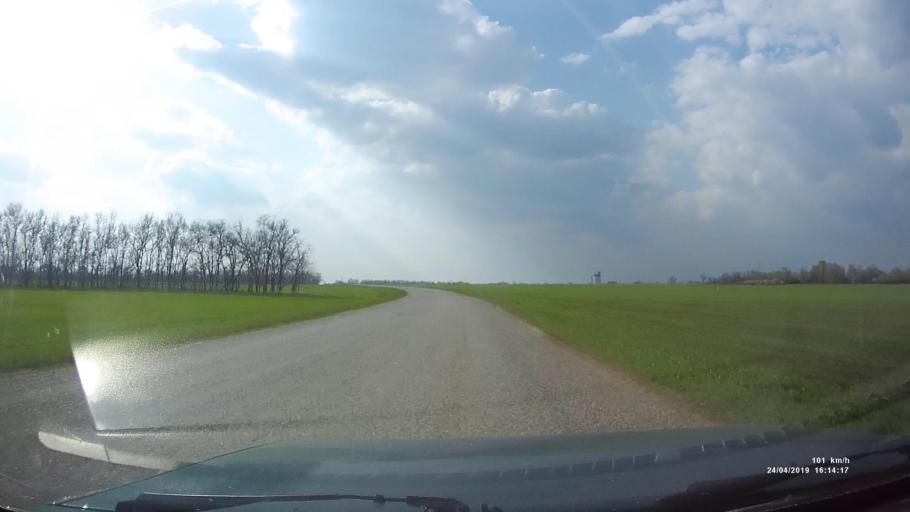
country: RU
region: Rostov
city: Sovetskoye
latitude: 46.7515
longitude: 42.2033
